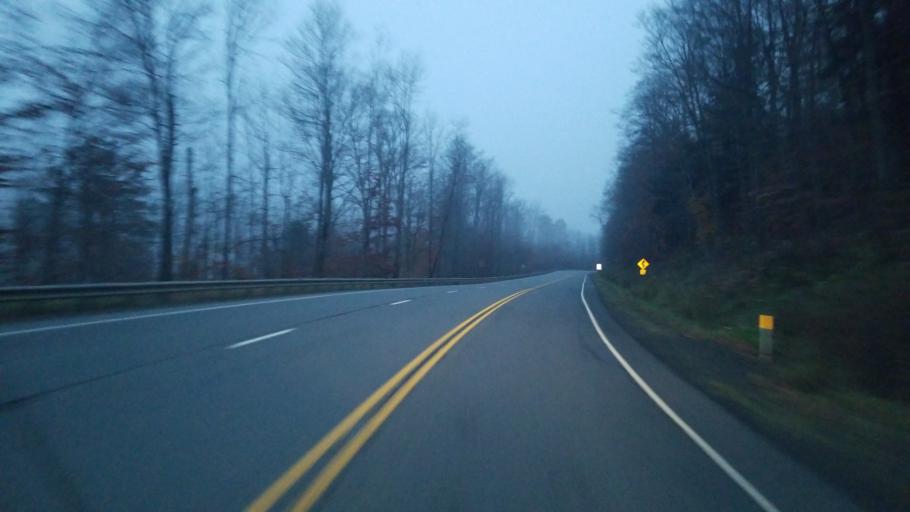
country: US
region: Pennsylvania
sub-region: McKean County
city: Smethport
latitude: 41.7177
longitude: -78.6087
